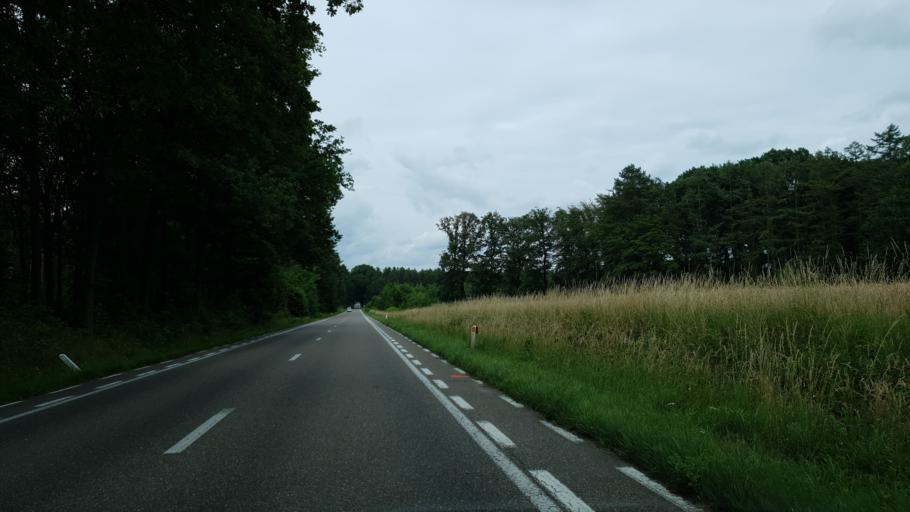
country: BE
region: Flanders
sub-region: Provincie Vlaams-Brabant
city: Scherpenheuvel-Zichem
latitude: 51.0398
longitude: 4.9839
